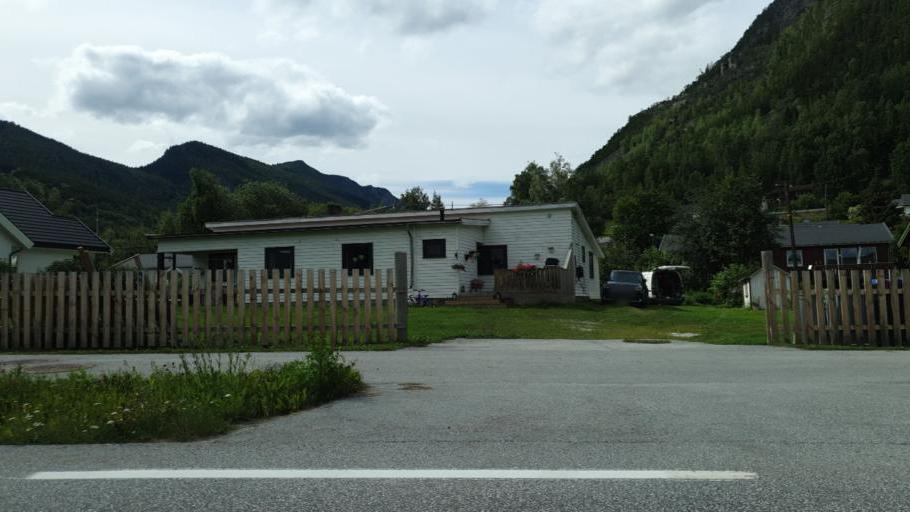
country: NO
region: Oppland
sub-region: Sel
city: Otta
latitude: 61.8425
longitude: 9.4126
